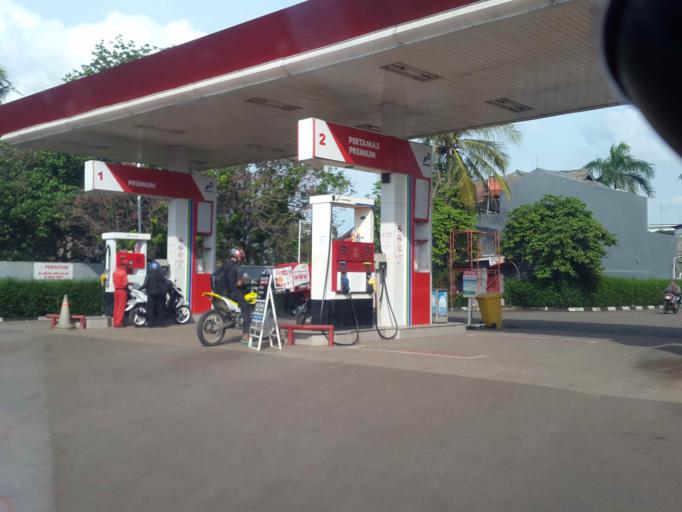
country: ID
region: Jakarta Raya
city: Jakarta
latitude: -6.2474
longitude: 106.9112
